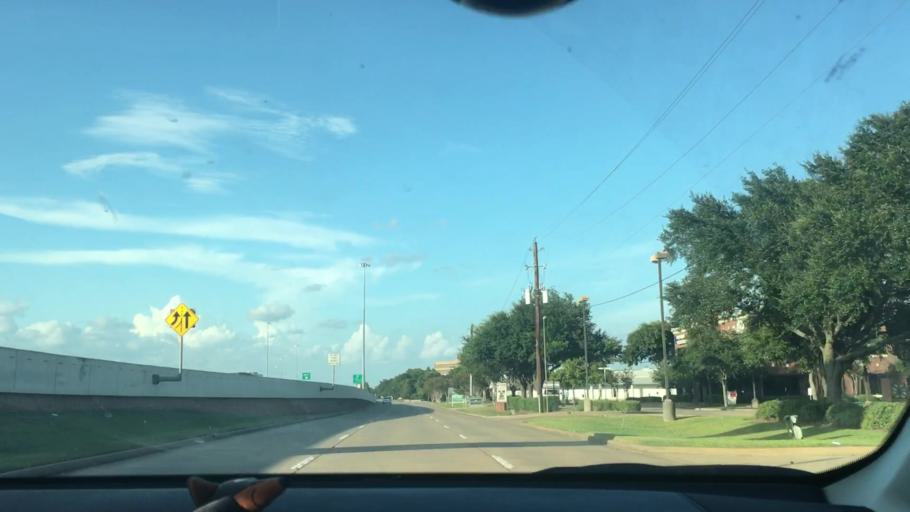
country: US
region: Texas
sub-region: Fort Bend County
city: Sugar Land
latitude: 29.6089
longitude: -95.6112
